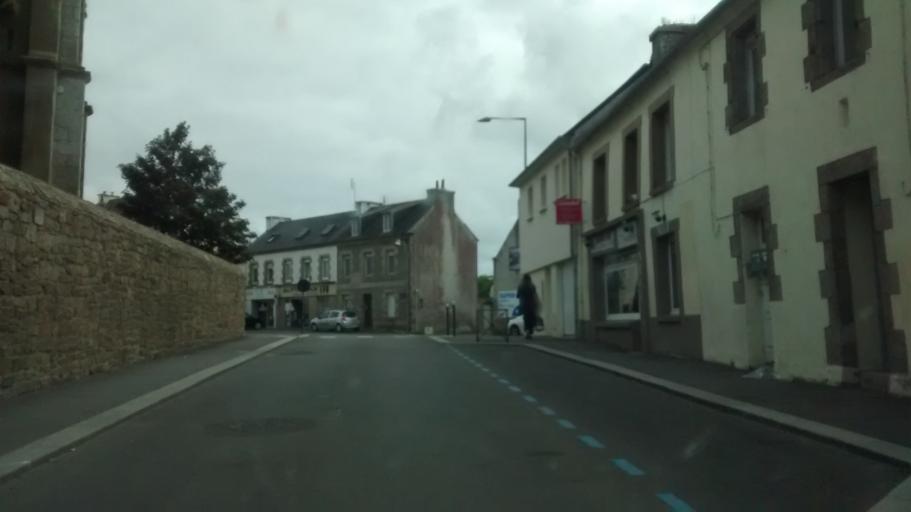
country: FR
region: Brittany
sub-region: Departement du Finistere
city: Plabennec
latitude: 48.5027
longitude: -4.4271
